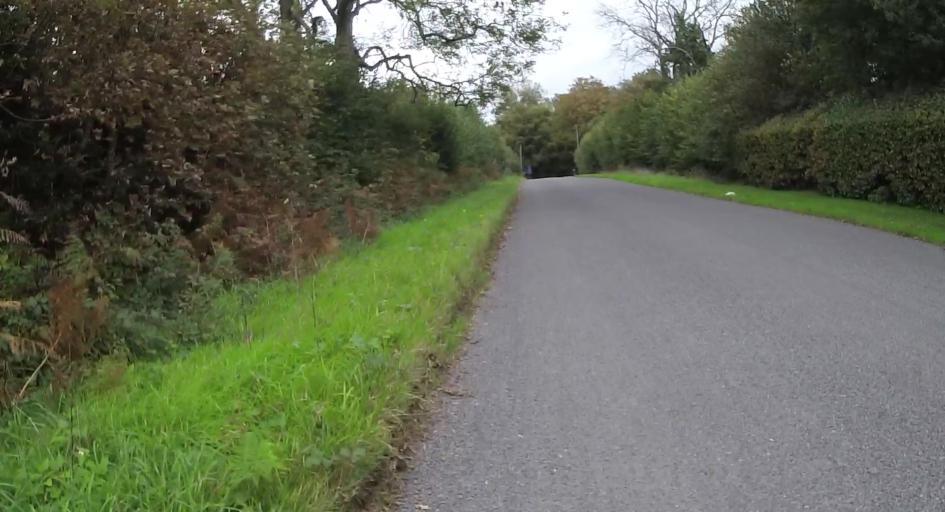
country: GB
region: England
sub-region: Hampshire
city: Four Marks
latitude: 51.1045
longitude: -1.0258
